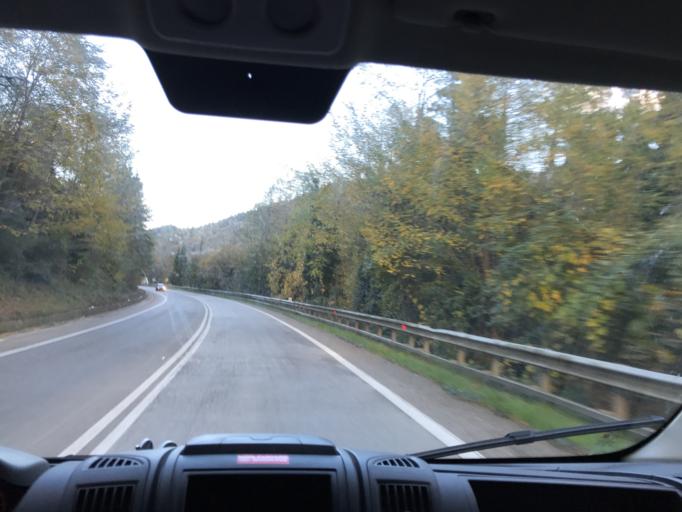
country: IT
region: The Marches
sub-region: Provincia di Ascoli Piceno
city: Marsia
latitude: 42.8096
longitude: 13.5008
